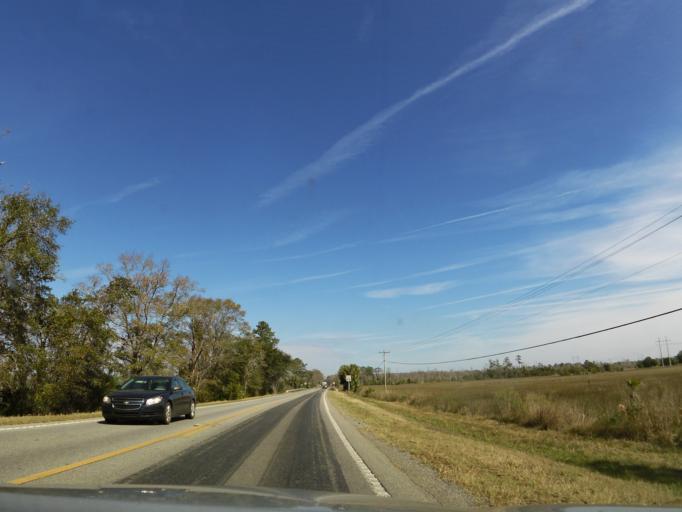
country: US
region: Georgia
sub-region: Glynn County
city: Dock Junction
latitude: 31.2638
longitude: -81.5949
